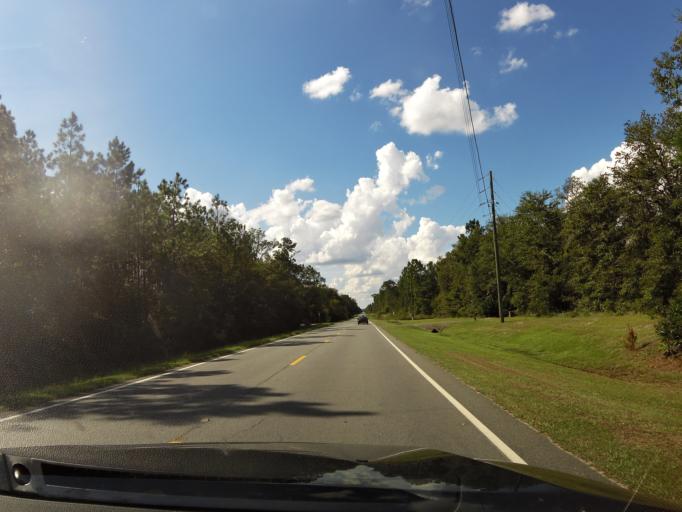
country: US
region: Georgia
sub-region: Lowndes County
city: Valdosta
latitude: 30.7871
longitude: -83.1712
